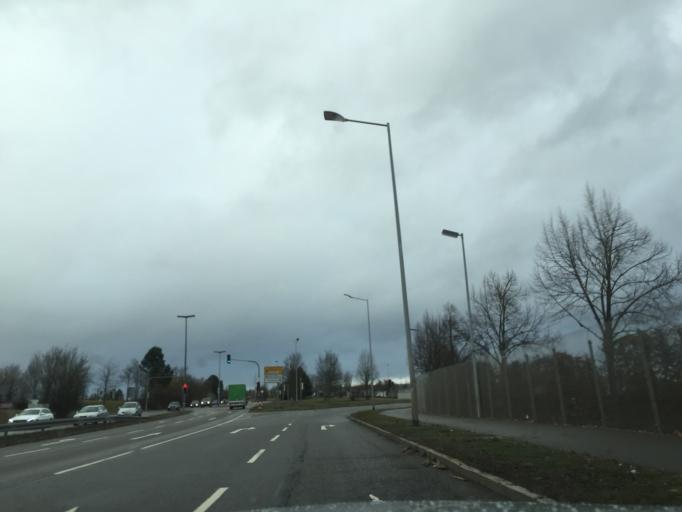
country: DE
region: Baden-Wuerttemberg
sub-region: Regierungsbezirk Stuttgart
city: Boeblingen
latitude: 48.6932
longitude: 8.9791
